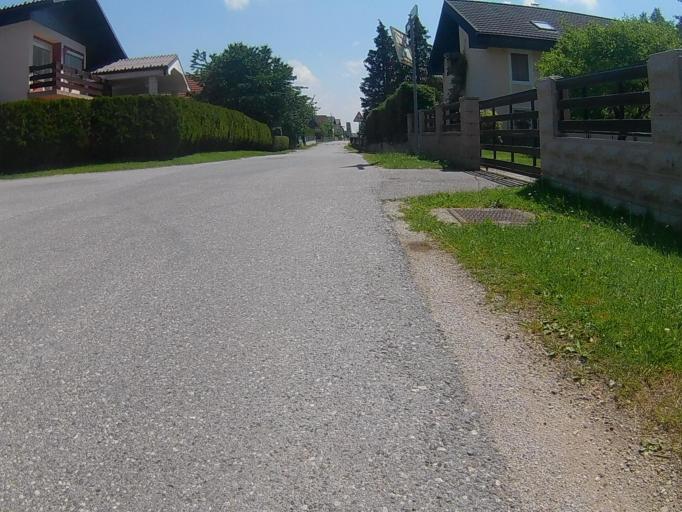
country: SI
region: Miklavz na Dravskem Polju
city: Miklavz na Dravskem Polju
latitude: 46.5063
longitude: 15.6929
